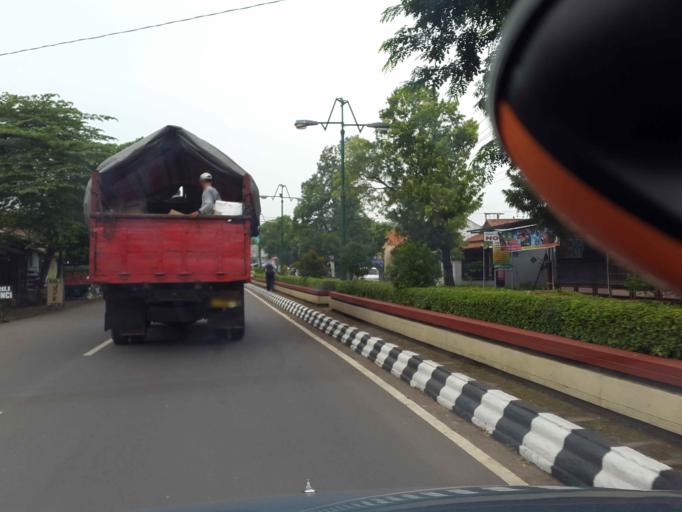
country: ID
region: Central Java
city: Kedungwuni
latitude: -6.9619
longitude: 109.6425
